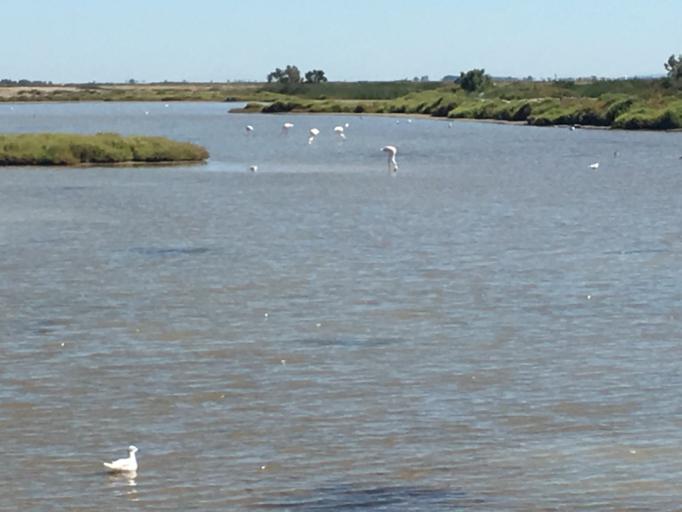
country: FR
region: Provence-Alpes-Cote d'Azur
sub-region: Departement des Bouches-du-Rhone
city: Saintes-Maries-de-la-Mer
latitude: 43.4574
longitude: 4.4314
